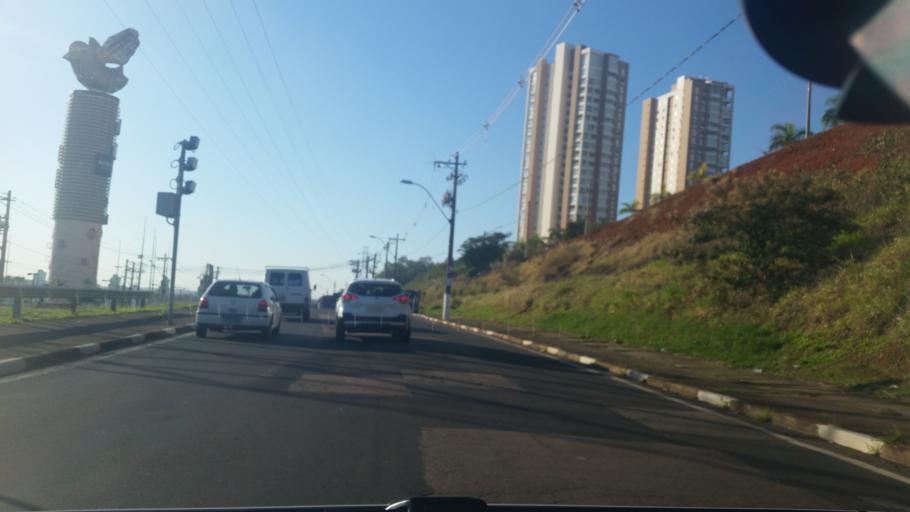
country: BR
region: Sao Paulo
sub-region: Campinas
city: Campinas
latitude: -22.8484
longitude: -47.0597
